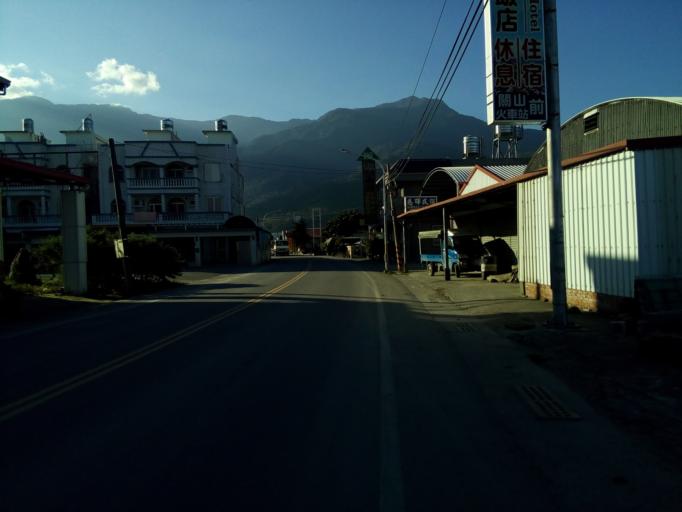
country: TW
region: Taiwan
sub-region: Taitung
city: Taitung
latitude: 23.0432
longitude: 121.1689
